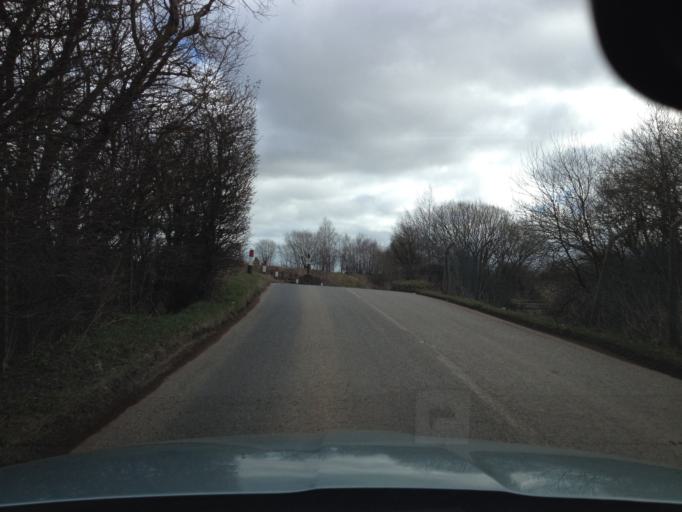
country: GB
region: Scotland
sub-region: West Lothian
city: Mid Calder
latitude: 55.9118
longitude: -3.4822
